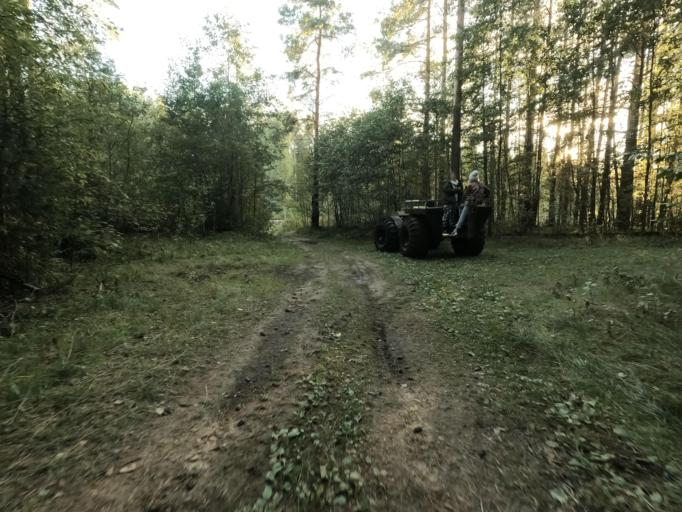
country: RU
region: Leningrad
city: Otradnoye
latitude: 59.8420
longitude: 30.7786
